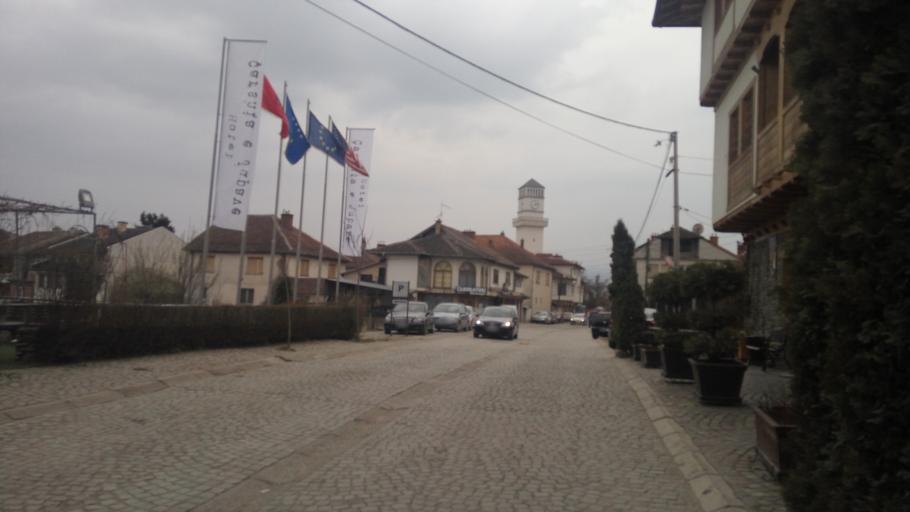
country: XK
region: Gjakova
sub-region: Komuna e Gjakoves
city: Gjakove
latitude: 42.3819
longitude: 20.4277
